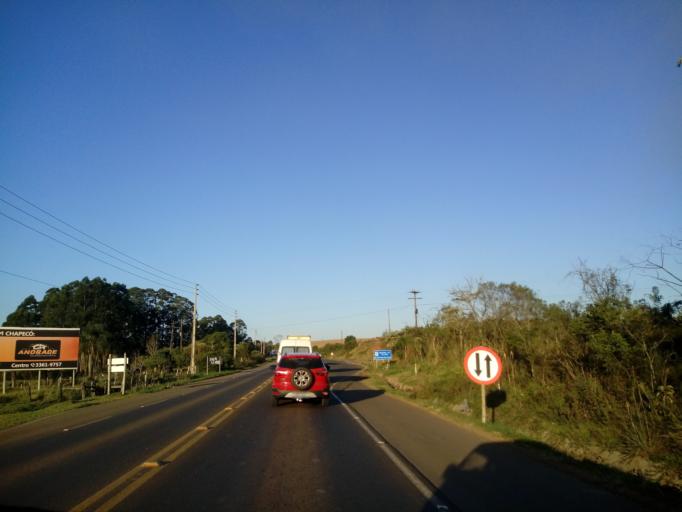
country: BR
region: Santa Catarina
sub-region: Chapeco
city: Chapeco
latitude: -27.2278
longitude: -52.6796
